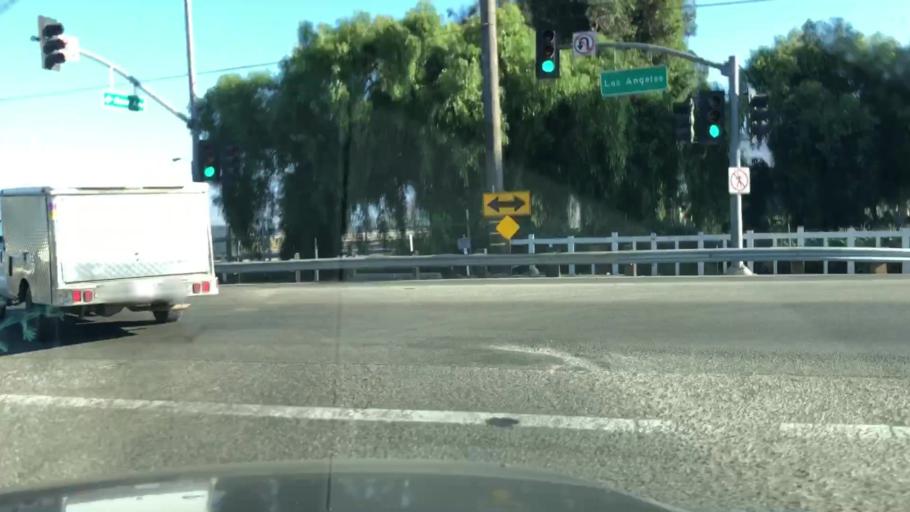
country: US
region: California
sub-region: Ventura County
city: Saticoy
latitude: 34.2679
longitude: -119.1266
